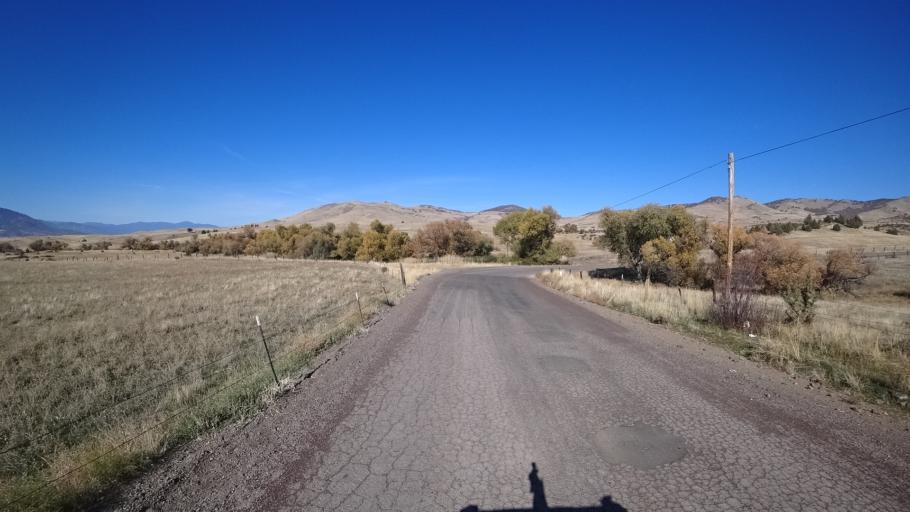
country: US
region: California
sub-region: Siskiyou County
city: Montague
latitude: 41.8146
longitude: -122.3766
